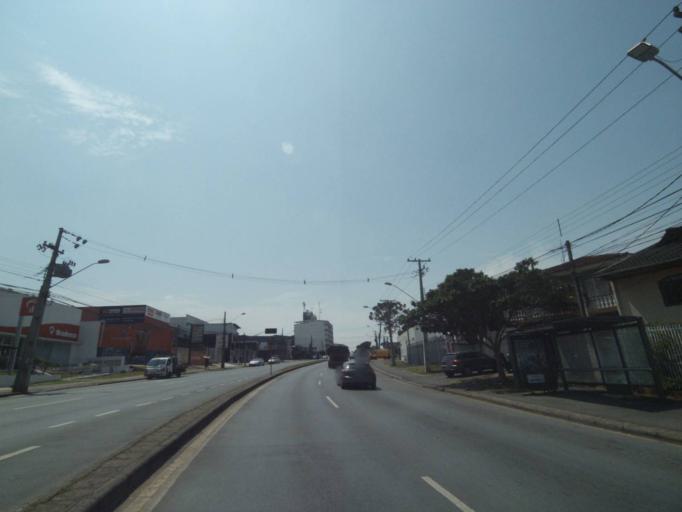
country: BR
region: Parana
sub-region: Curitiba
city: Curitiba
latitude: -25.4788
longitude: -49.3136
